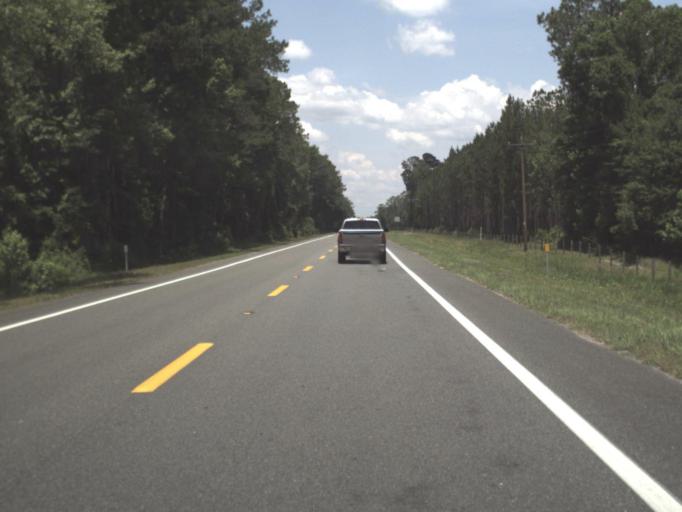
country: US
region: Florida
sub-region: Union County
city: Lake Butler
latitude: 30.0519
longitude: -82.4068
